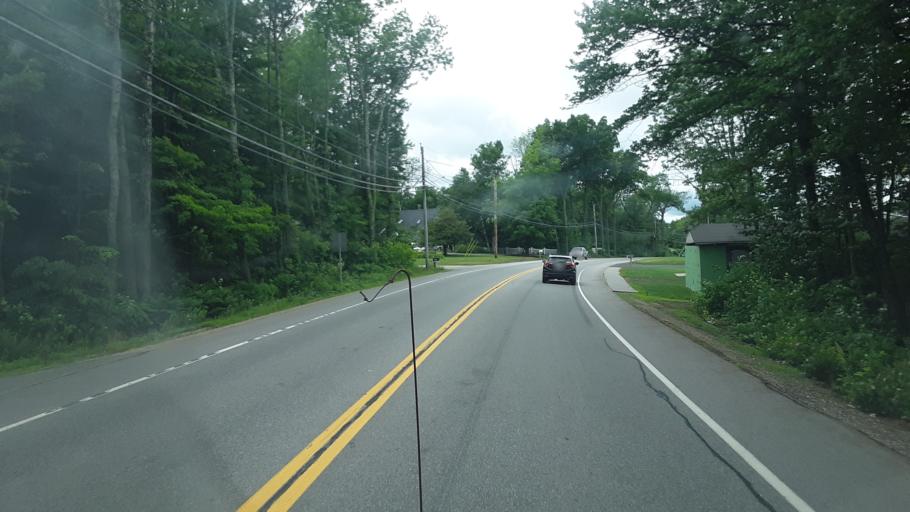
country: US
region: New Hampshire
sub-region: Rockingham County
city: Northwood
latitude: 43.2092
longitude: -71.1839
